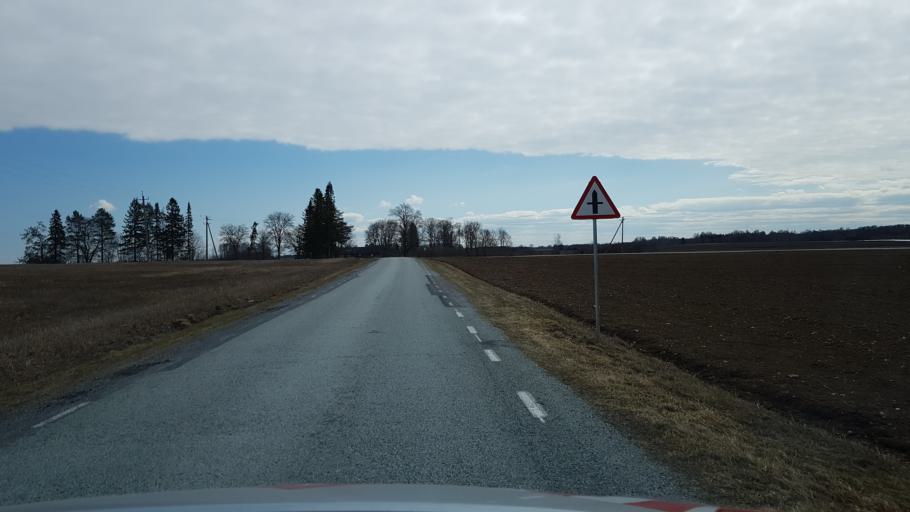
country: EE
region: Laeaene-Virumaa
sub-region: Haljala vald
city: Haljala
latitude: 59.4253
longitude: 26.2235
